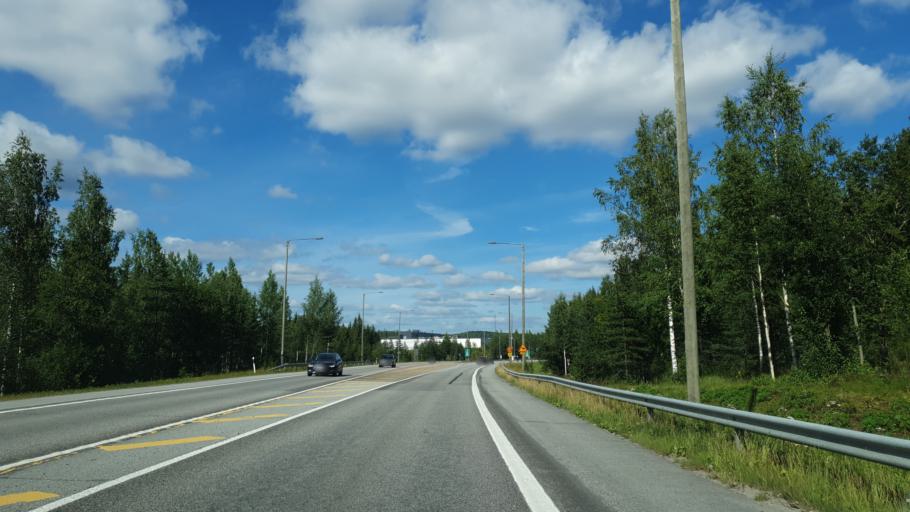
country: FI
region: Central Finland
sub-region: Jyvaeskylae
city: Muurame
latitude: 62.1783
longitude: 25.6809
